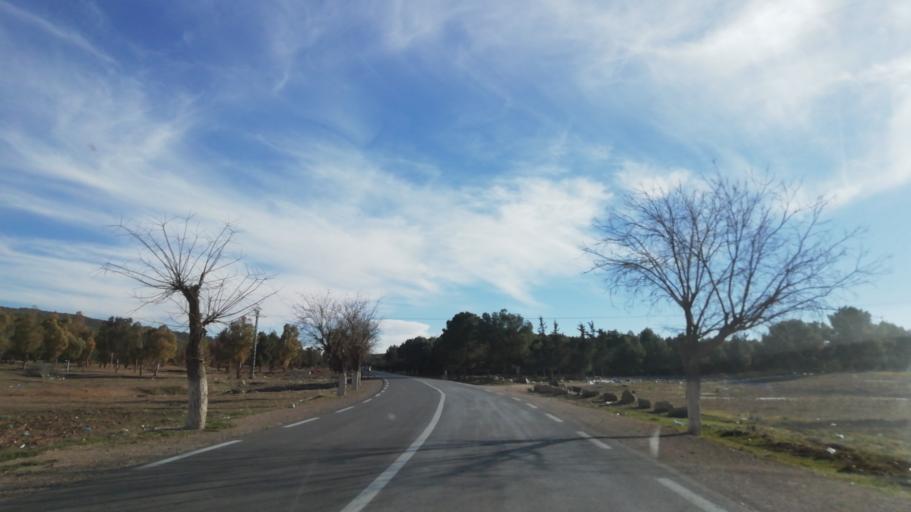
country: DZ
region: Tlemcen
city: Sebdou
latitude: 34.6195
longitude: -1.3350
